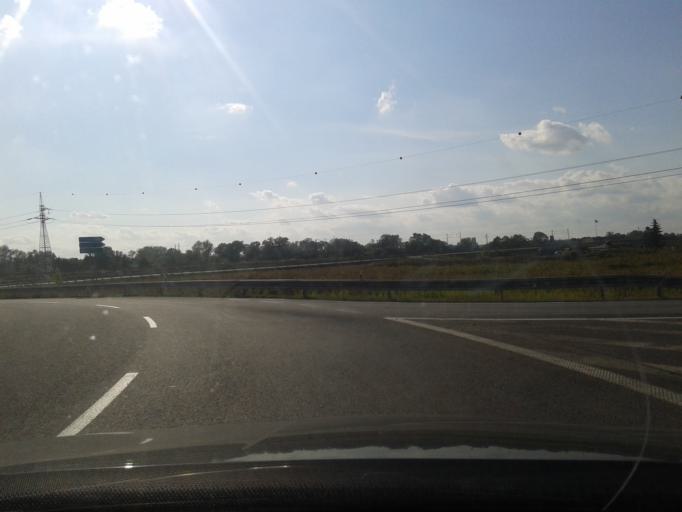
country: CZ
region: Moravskoslezsky
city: Stary Bohumin
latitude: 49.9110
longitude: 18.3347
